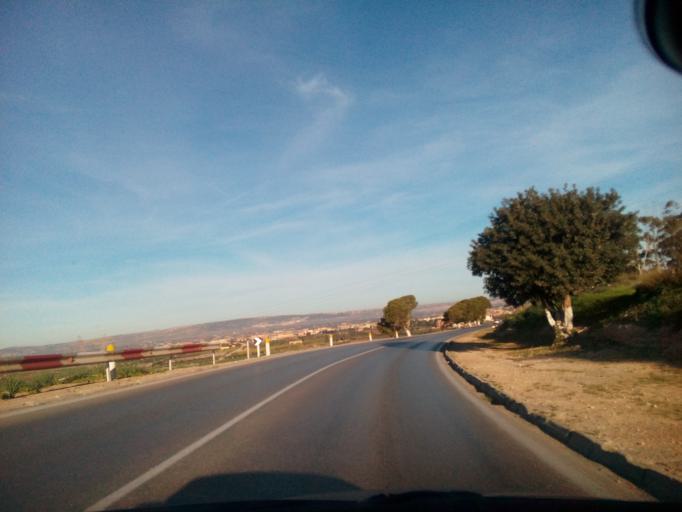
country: DZ
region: Mostaganem
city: Mostaganem
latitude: 35.7653
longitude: 0.2007
